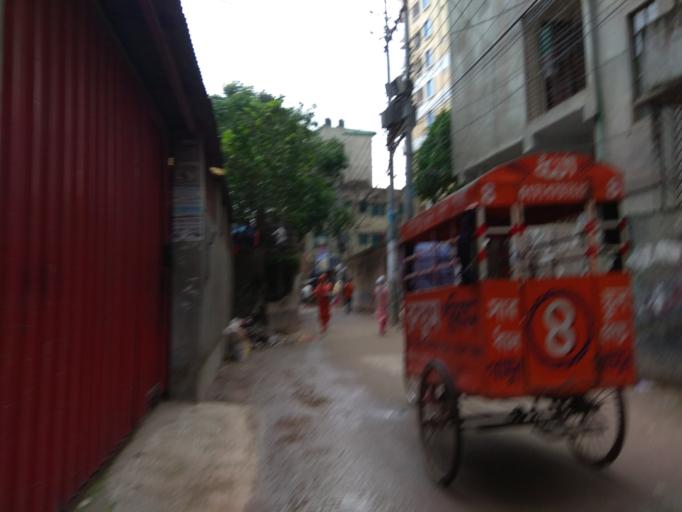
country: BD
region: Dhaka
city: Azimpur
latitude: 23.7931
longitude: 90.3693
